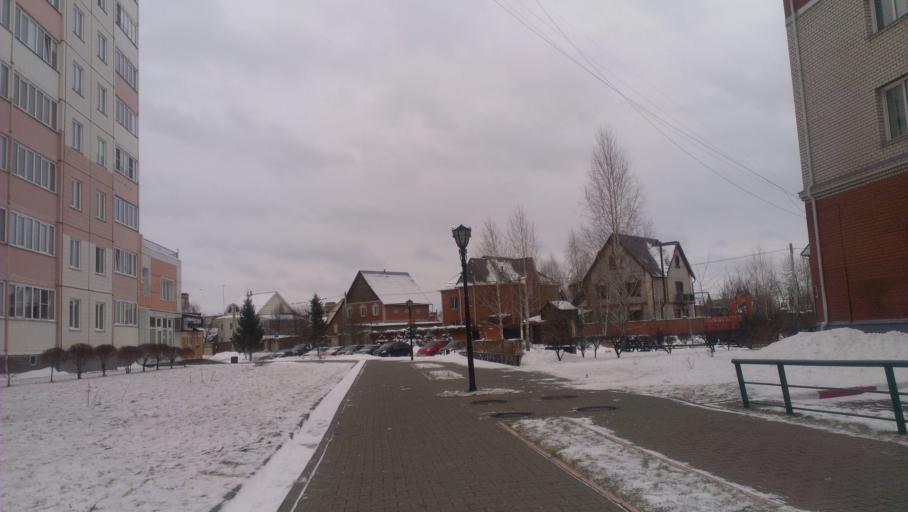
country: RU
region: Altai Krai
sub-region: Gorod Barnaulskiy
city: Barnaul
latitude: 53.3568
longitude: 83.6932
